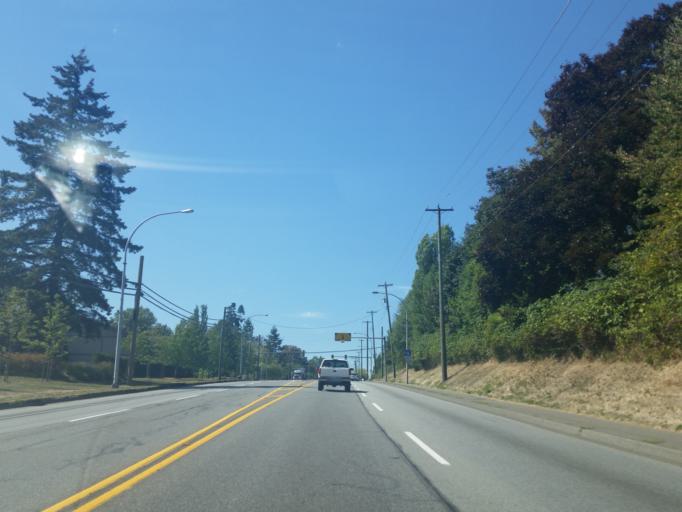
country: CA
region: British Columbia
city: Langley
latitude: 49.1042
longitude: -122.6988
